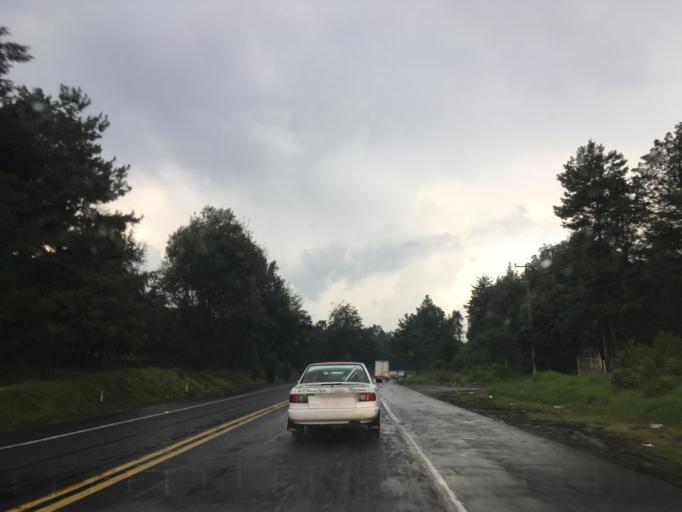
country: MX
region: Michoacan
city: Capacuaro
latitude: 19.5271
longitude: -102.0769
